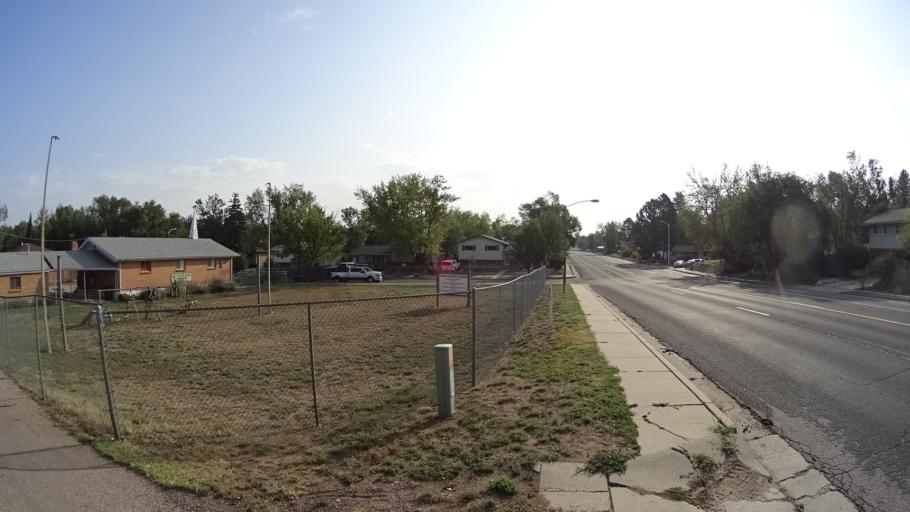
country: US
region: Colorado
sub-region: El Paso County
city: Colorado Springs
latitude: 38.8543
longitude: -104.7920
